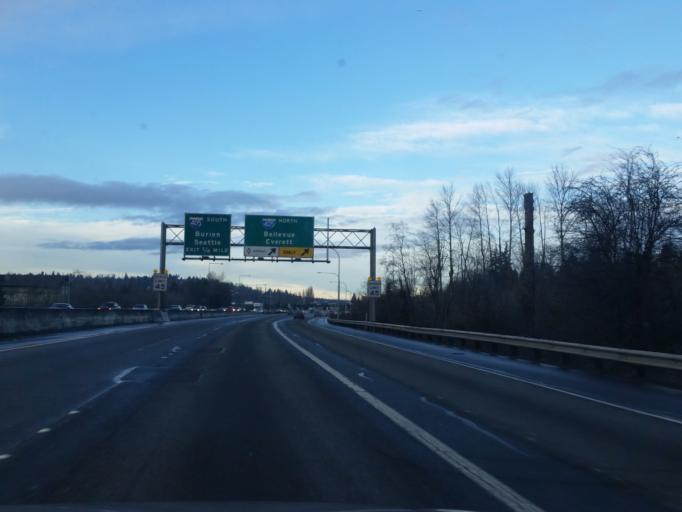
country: US
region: Washington
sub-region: King County
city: Renton
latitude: 47.4616
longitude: -122.2177
